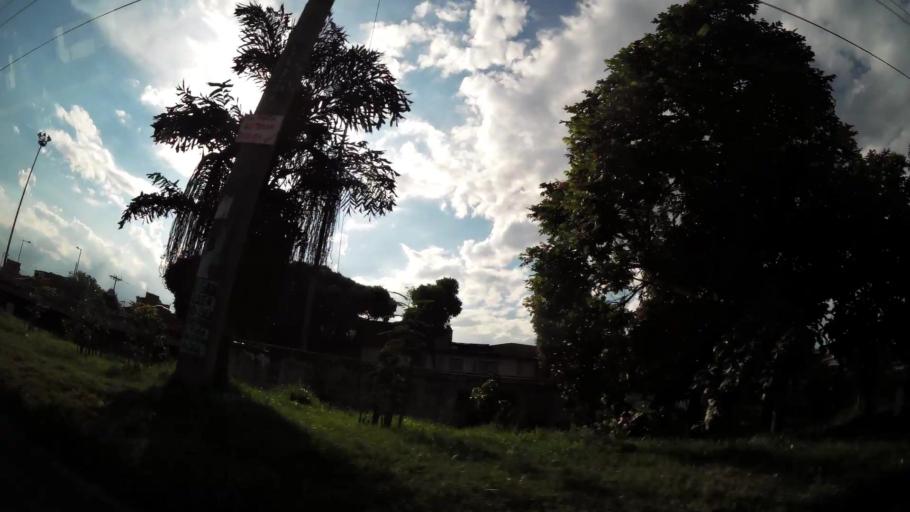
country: CO
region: Valle del Cauca
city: Cali
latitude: 3.4228
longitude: -76.4860
